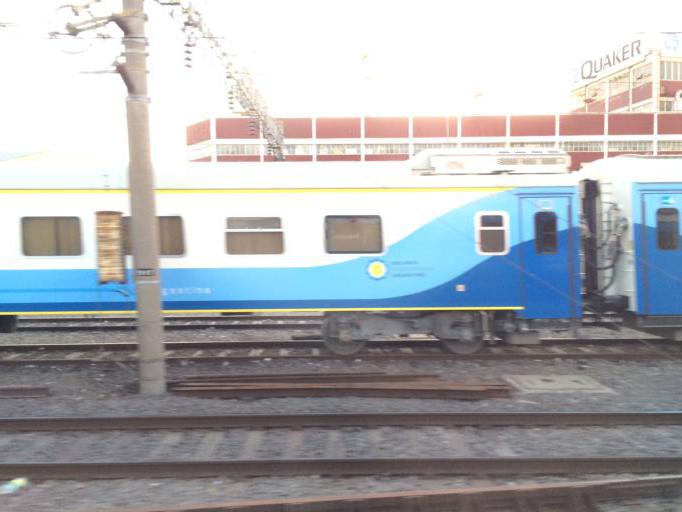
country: AR
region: Buenos Aires F.D.
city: Buenos Aires
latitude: -34.6369
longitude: -58.3806
